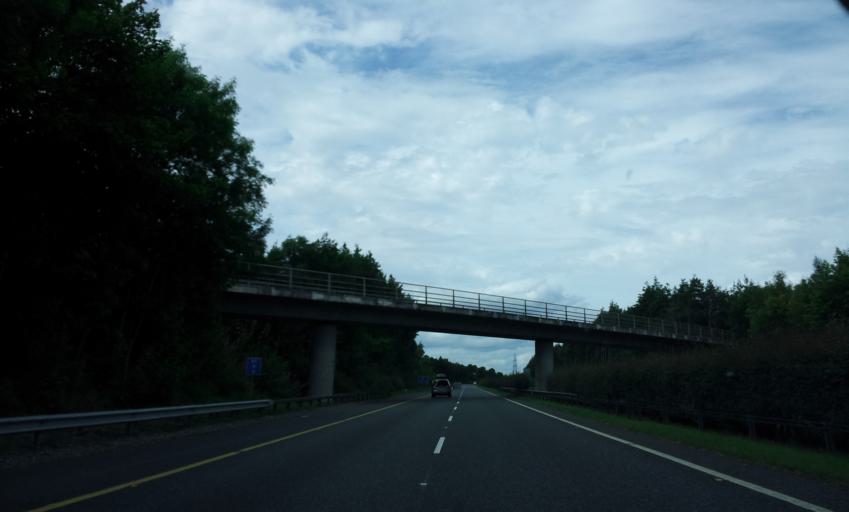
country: IE
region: Leinster
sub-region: Kildare
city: Kilcullen
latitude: 53.1266
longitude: -6.7606
